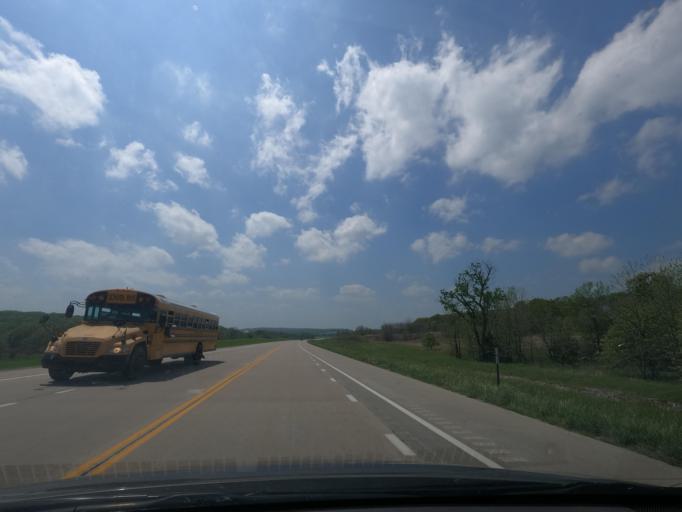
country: US
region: Kansas
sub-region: Wilson County
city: Fredonia
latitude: 37.6136
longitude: -95.9303
